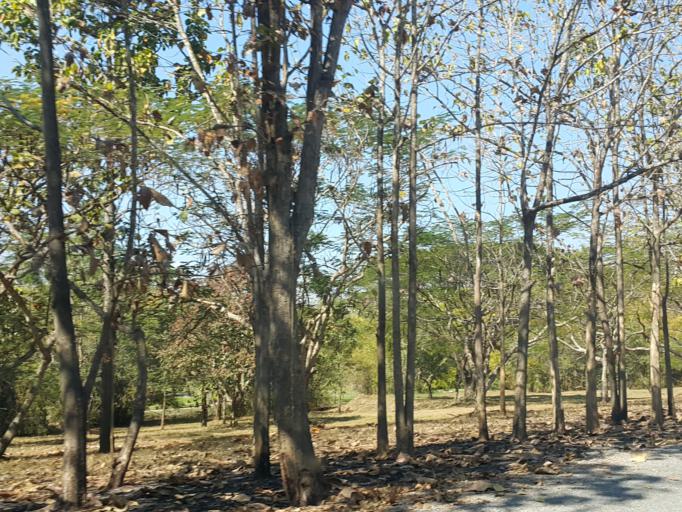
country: TH
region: Chiang Mai
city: Mae Taeng
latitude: 19.0303
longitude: 98.9909
